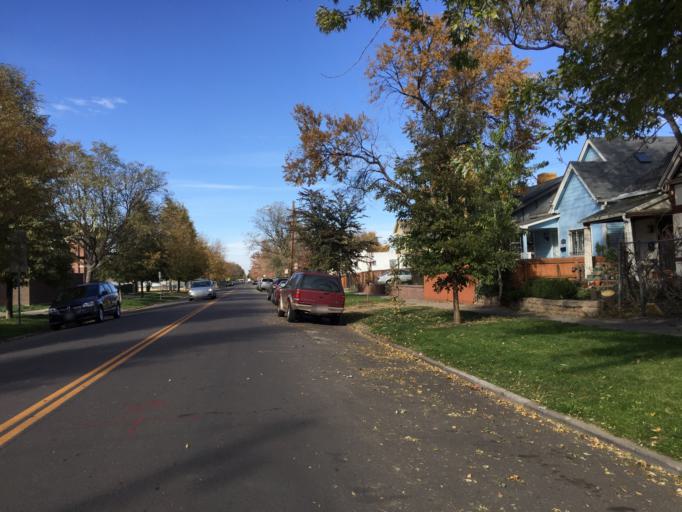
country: US
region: Colorado
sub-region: Denver County
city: Denver
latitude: 39.7621
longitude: -104.9684
